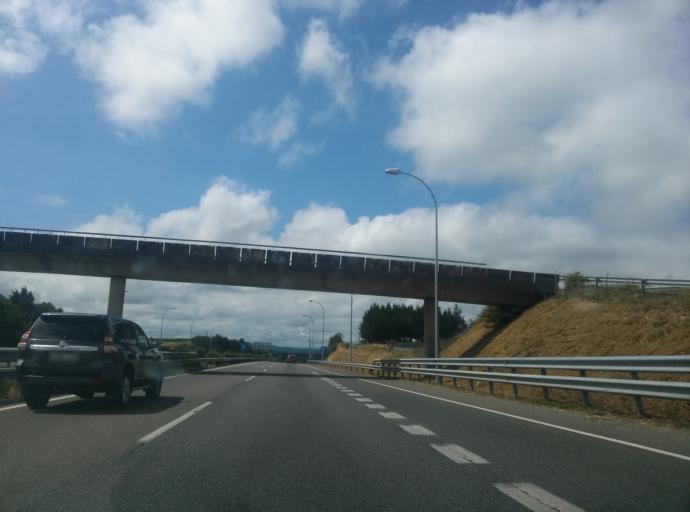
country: ES
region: Galicia
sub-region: Provincia de Lugo
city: Lugo
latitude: 43.0594
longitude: -7.5619
